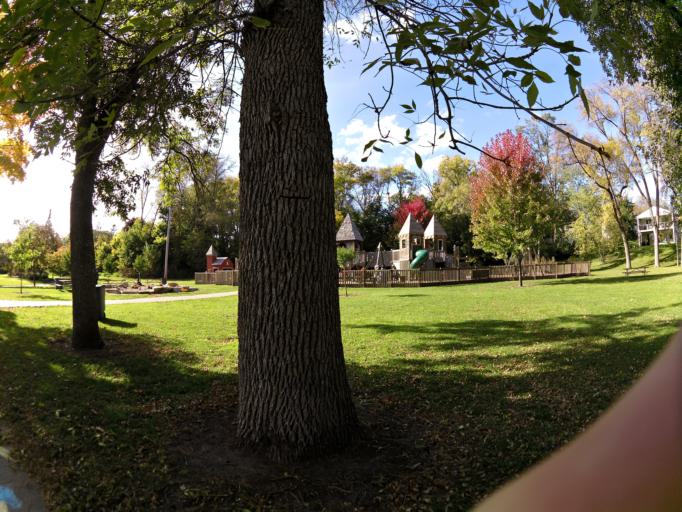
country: US
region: Minnesota
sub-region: Olmsted County
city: Rochester
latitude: 44.0159
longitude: -92.4683
